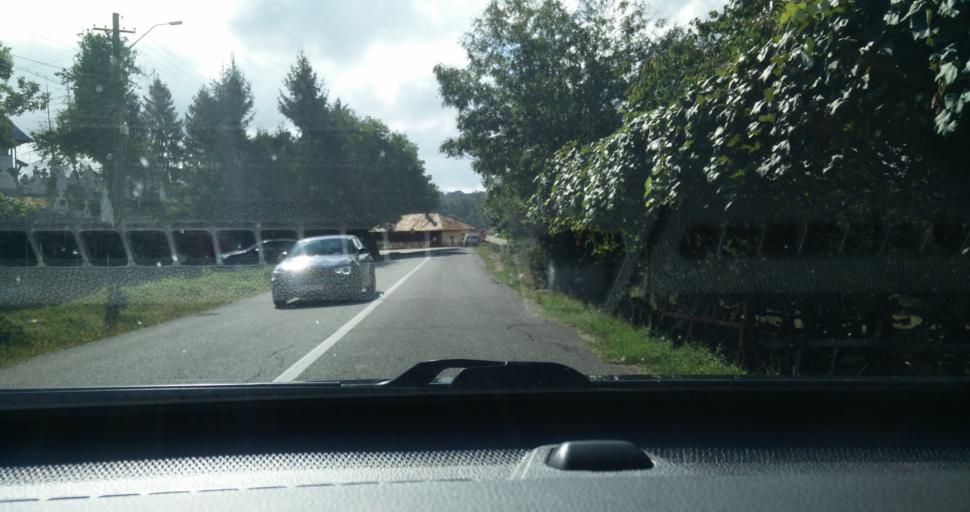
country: RO
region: Gorj
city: Novaci-Straini
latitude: 45.1813
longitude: 23.6799
